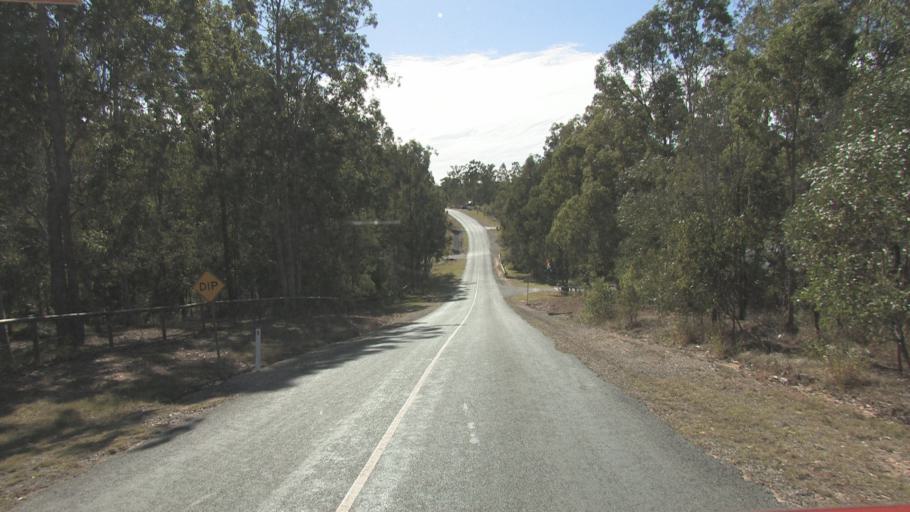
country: AU
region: Queensland
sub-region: Ipswich
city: Springfield Lakes
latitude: -27.7181
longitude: 152.9148
